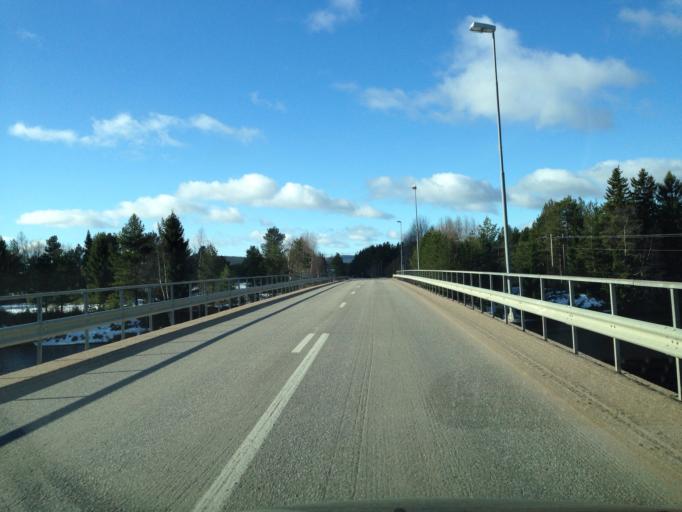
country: SE
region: Jaemtland
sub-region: Harjedalens Kommun
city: Sveg
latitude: 62.0468
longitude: 14.6487
